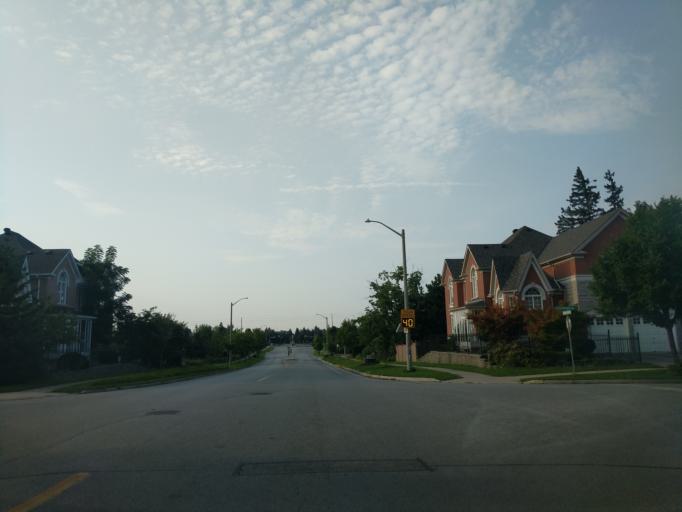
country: CA
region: Ontario
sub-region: York
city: Richmond Hill
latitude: 43.8796
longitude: -79.4076
